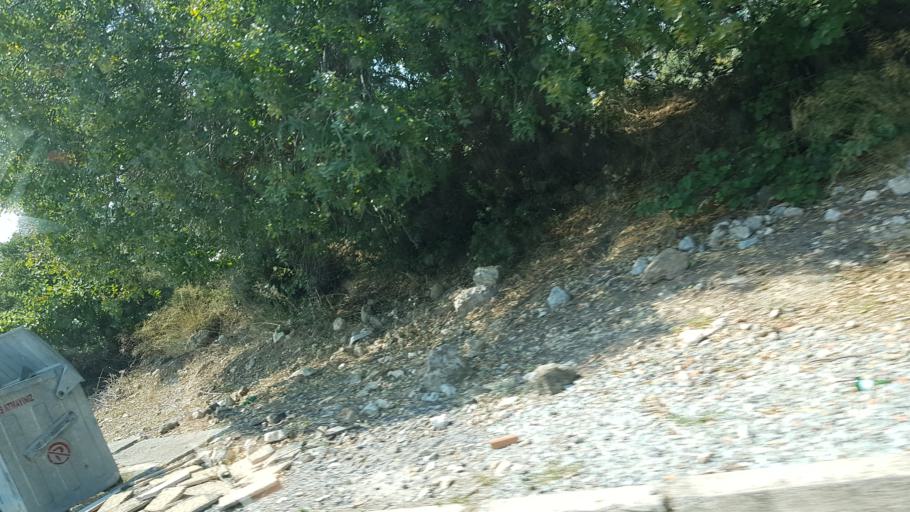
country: TR
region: Izmir
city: Urla
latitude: 38.3814
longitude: 26.7456
